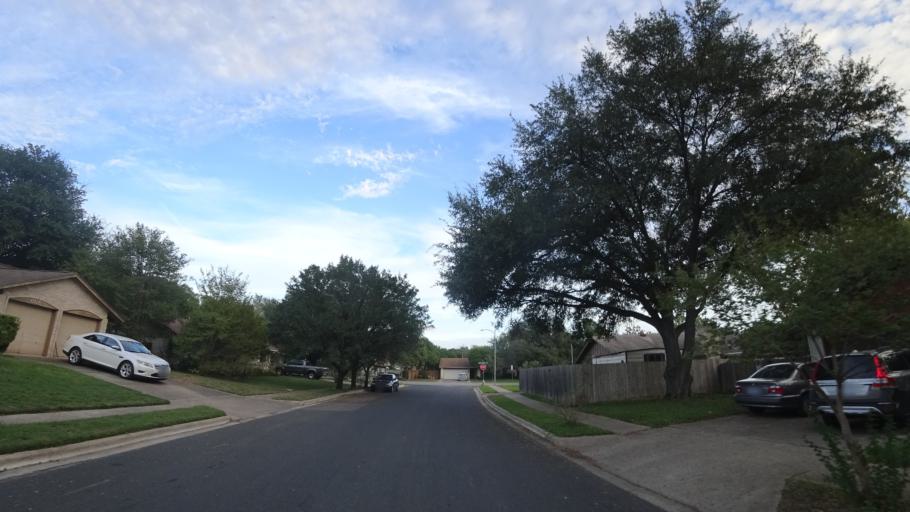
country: US
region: Texas
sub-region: Travis County
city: Austin
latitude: 30.2061
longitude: -97.7659
